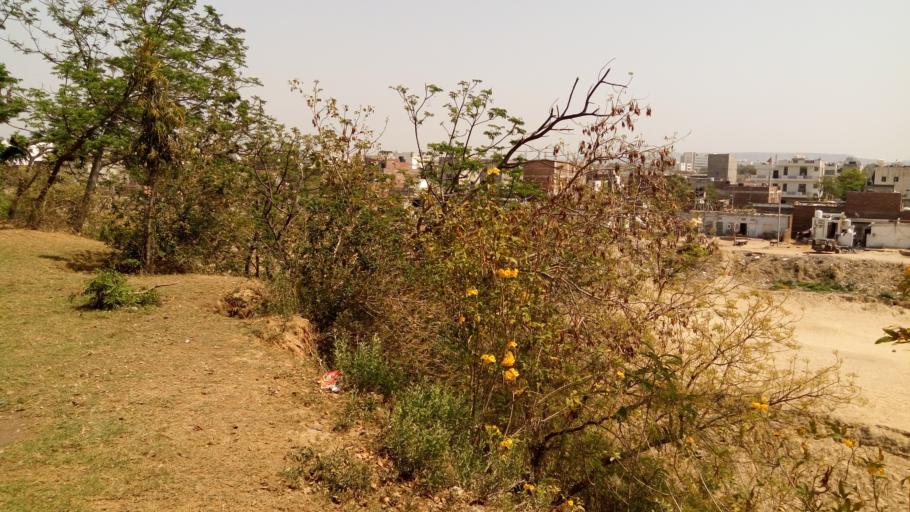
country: IN
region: Rajasthan
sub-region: Jaipur
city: Jaipur
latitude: 26.8597
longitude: 75.7738
